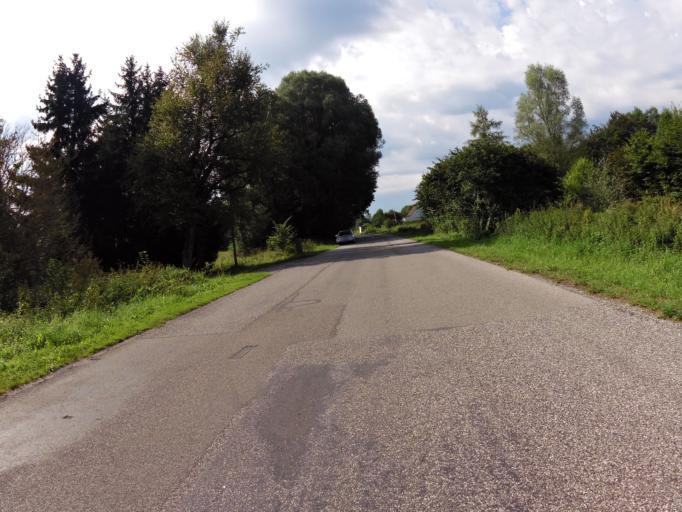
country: DE
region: Bavaria
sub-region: Upper Bavaria
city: Diessen am Ammersee
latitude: 47.9419
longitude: 11.1068
